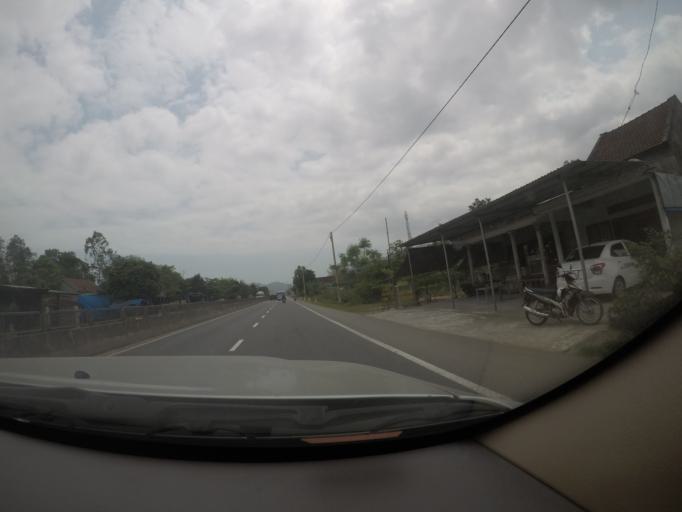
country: VN
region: Thua Thien-Hue
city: Phu Loc
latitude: 16.2717
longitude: 107.9804
